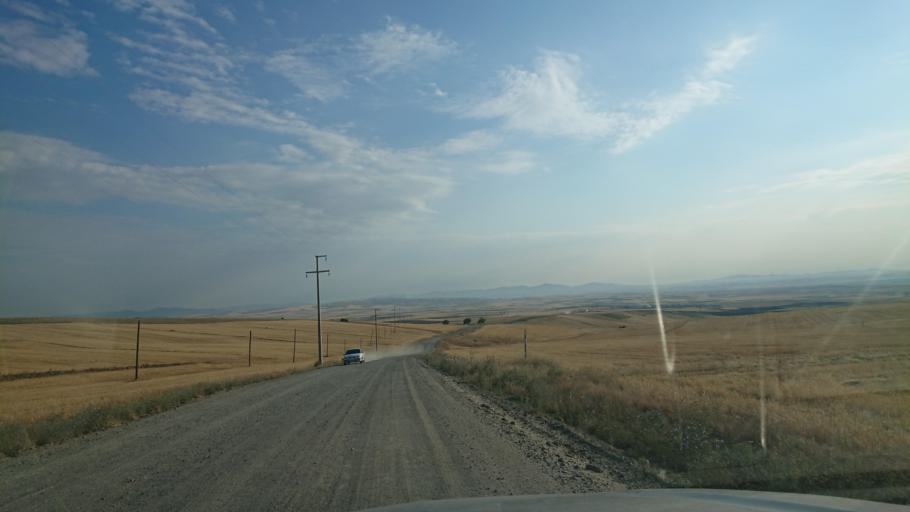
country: TR
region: Aksaray
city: Ortakoy
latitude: 38.7877
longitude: 34.0637
